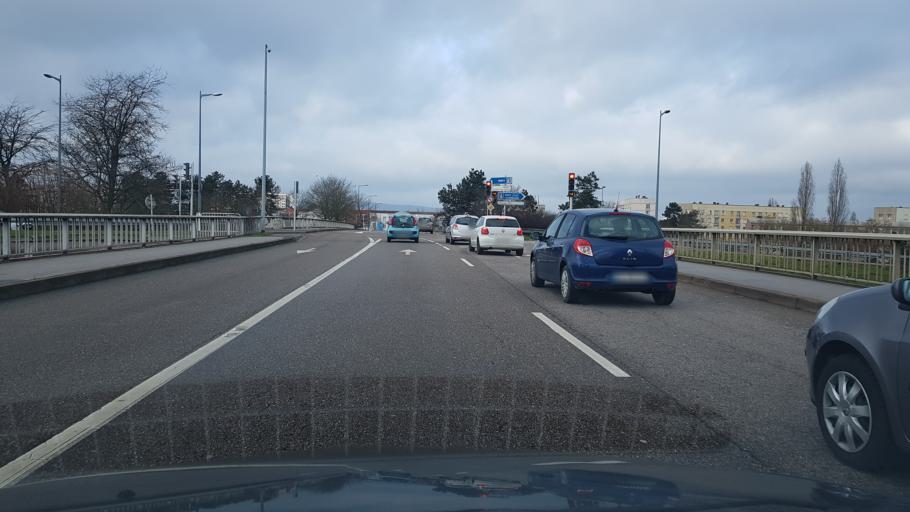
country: FR
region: Lorraine
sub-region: Departement de la Moselle
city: Metz
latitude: 49.1313
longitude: 6.1718
